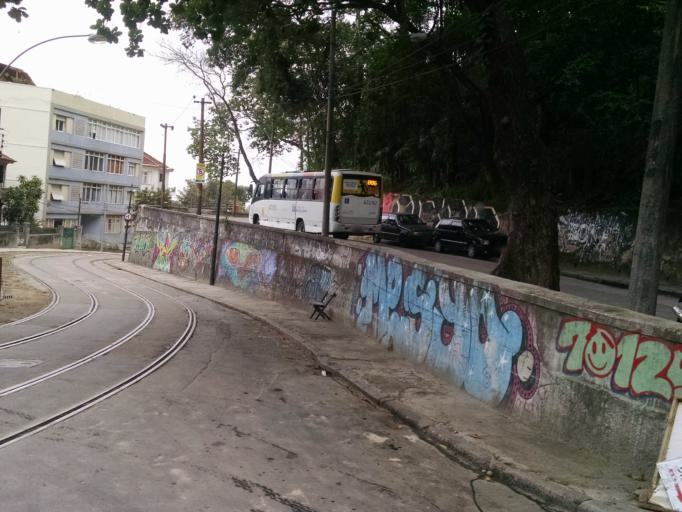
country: BR
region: Rio de Janeiro
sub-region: Rio De Janeiro
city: Rio de Janeiro
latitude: -22.9240
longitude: -43.1874
